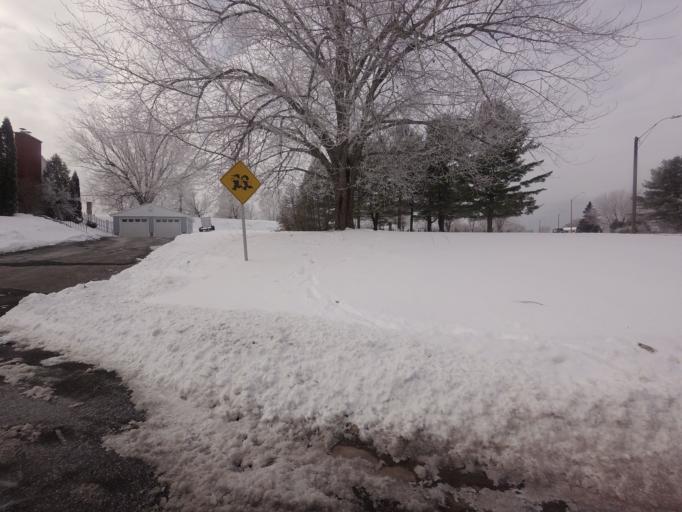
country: CA
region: New Brunswick
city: Oromocto
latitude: 45.8493
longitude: -66.4876
